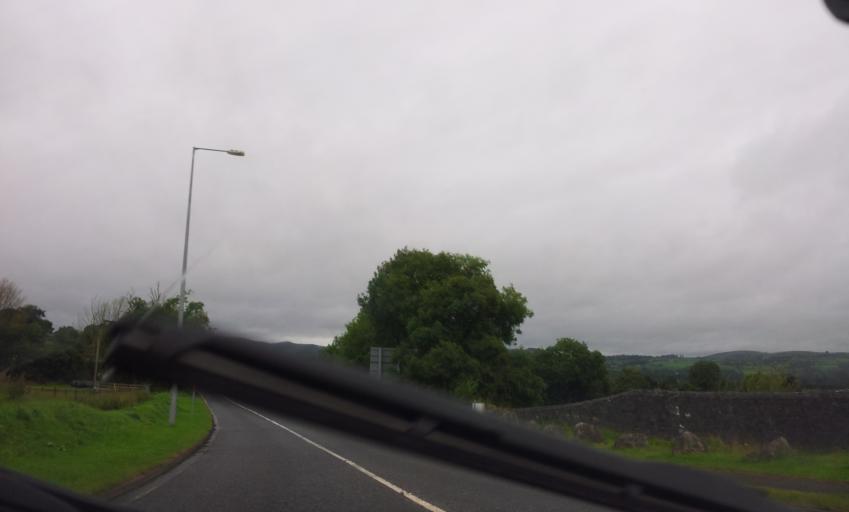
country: IE
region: Munster
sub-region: County Cork
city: Mitchelstown
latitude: 52.2649
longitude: -8.2913
